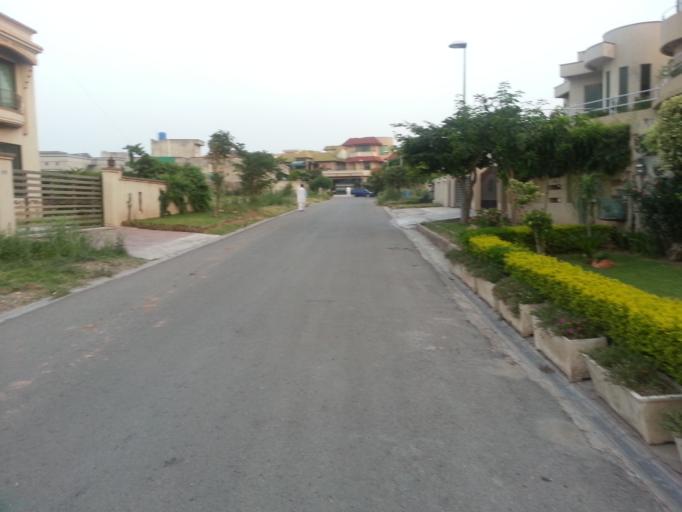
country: PK
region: Punjab
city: Rawalpindi
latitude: 33.5411
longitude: 73.0940
